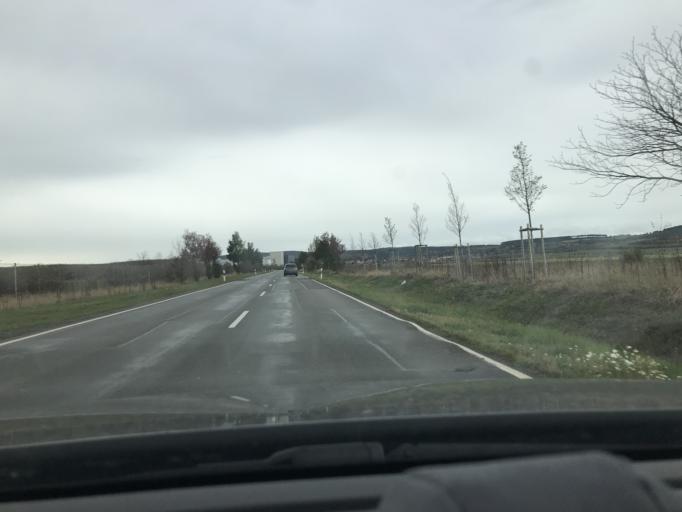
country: DE
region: Thuringia
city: Arnstadt
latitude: 50.8670
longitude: 10.9433
